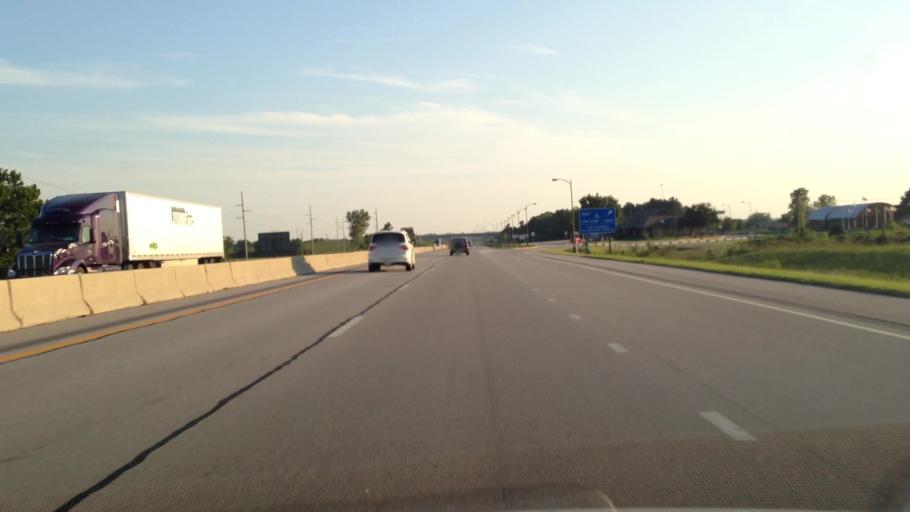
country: US
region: Oklahoma
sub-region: Ottawa County
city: Miami
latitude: 36.8775
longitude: -94.8445
